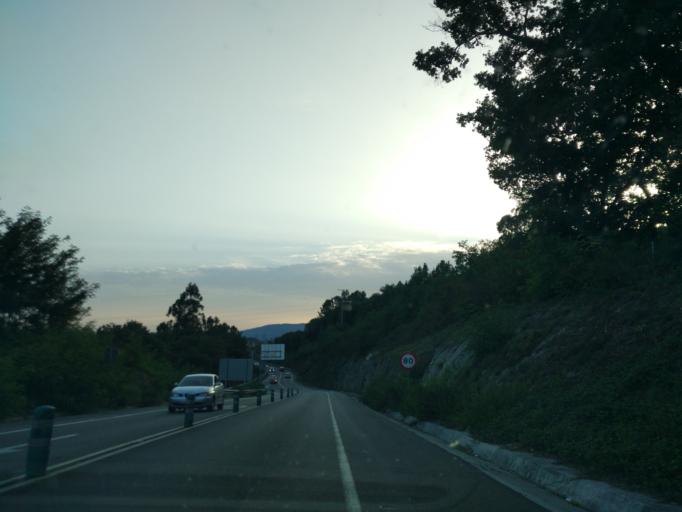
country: ES
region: Galicia
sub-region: Provincia da Coruna
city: Padron
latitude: 42.7315
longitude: -8.6457
